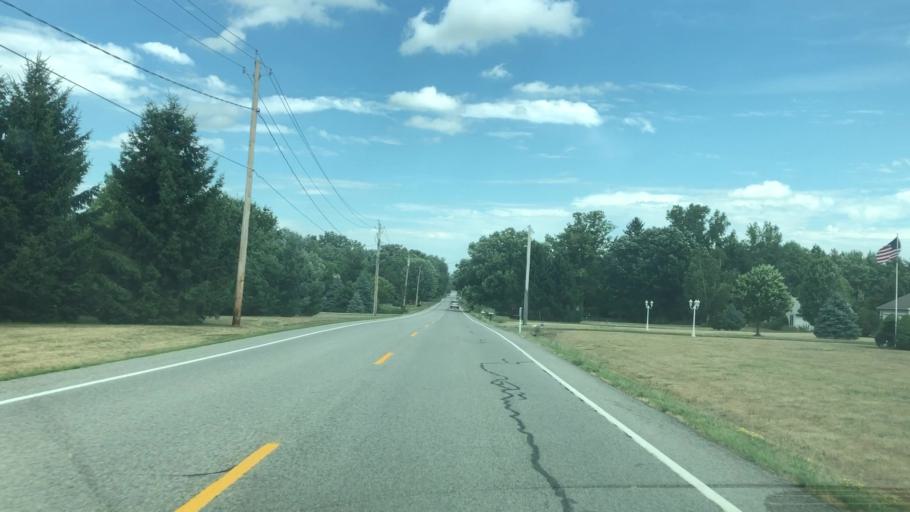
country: US
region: New York
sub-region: Wayne County
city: Macedon
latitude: 43.1110
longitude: -77.3523
